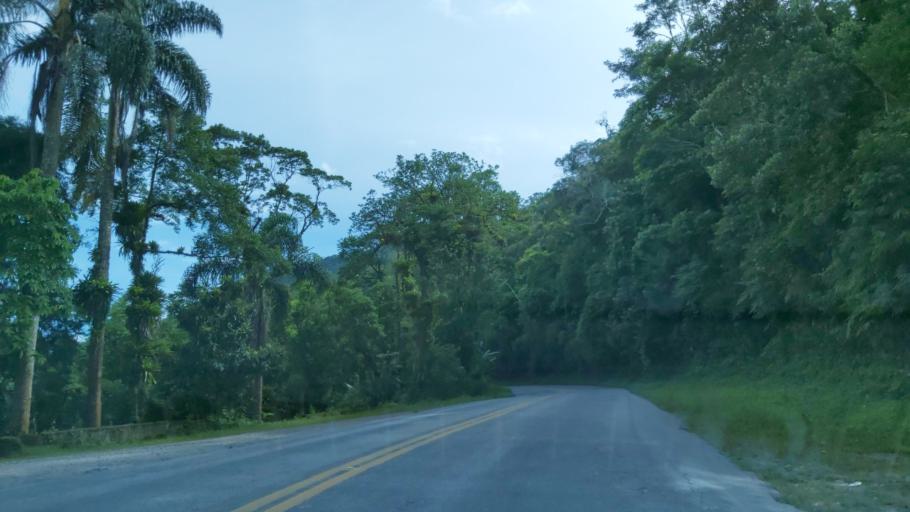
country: BR
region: Sao Paulo
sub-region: Miracatu
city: Miracatu
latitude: -24.0478
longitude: -47.5701
